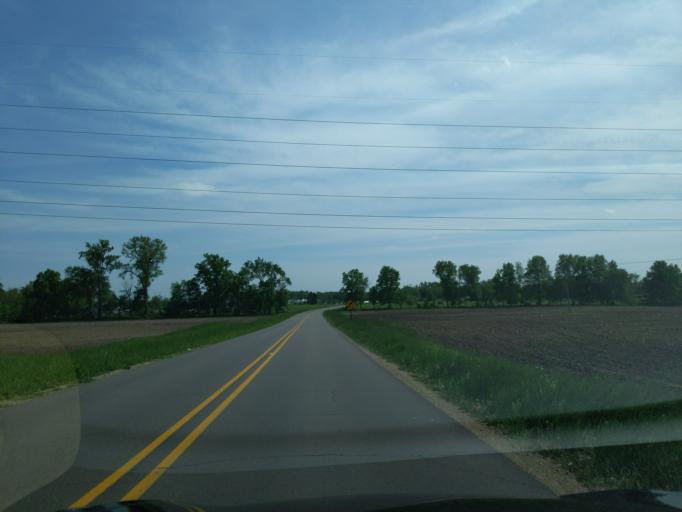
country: US
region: Michigan
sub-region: Ingham County
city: Leslie
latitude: 42.4187
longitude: -84.3124
